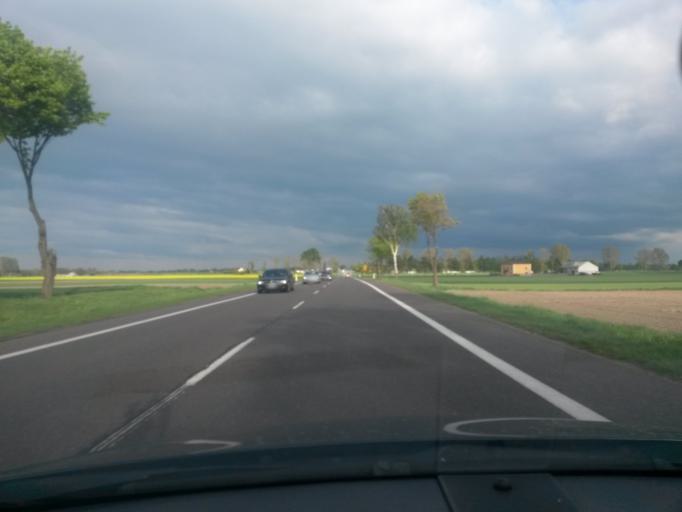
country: PL
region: Masovian Voivodeship
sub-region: Powiat plocki
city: Bulkowo
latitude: 52.6410
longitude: 20.1292
